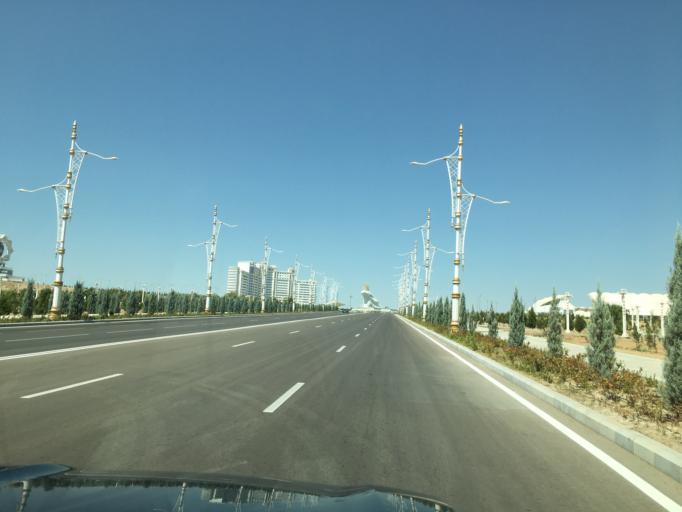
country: TM
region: Ahal
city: Ashgabat
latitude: 37.9220
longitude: 58.3508
